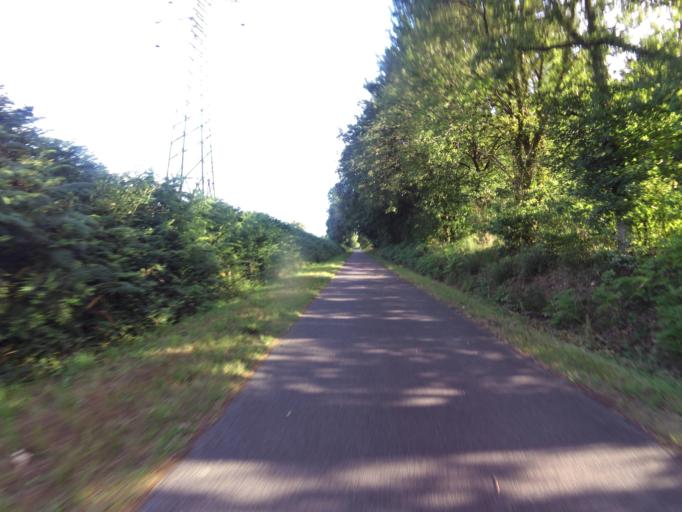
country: FR
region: Brittany
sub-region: Departement du Morbihan
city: Guillac
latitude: 47.9014
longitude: -2.4345
